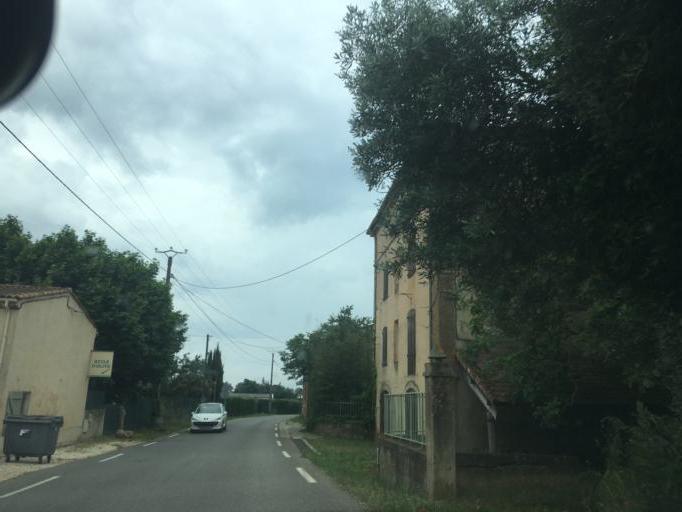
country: FR
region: Provence-Alpes-Cote d'Azur
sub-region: Departement du Var
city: La Londe-les-Maures
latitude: 43.1494
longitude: 6.2281
